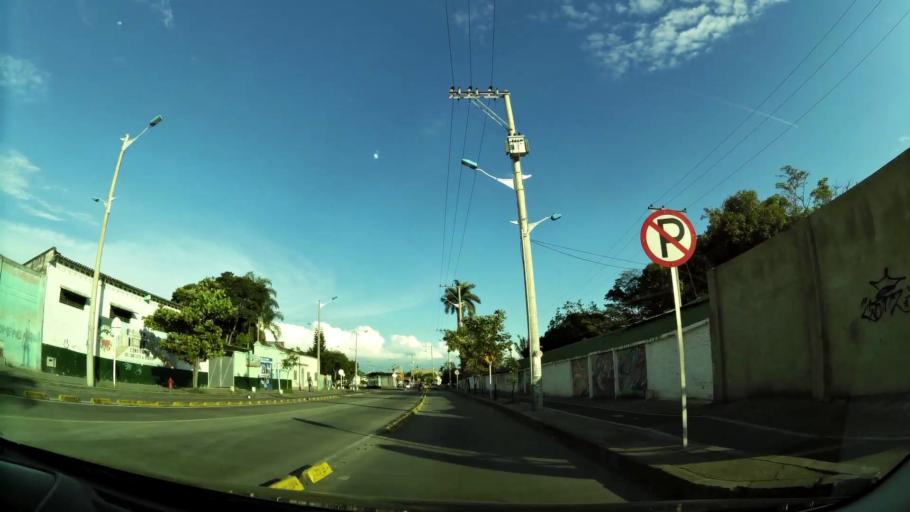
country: CO
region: Valle del Cauca
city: Cali
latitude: 3.4326
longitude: -76.5114
